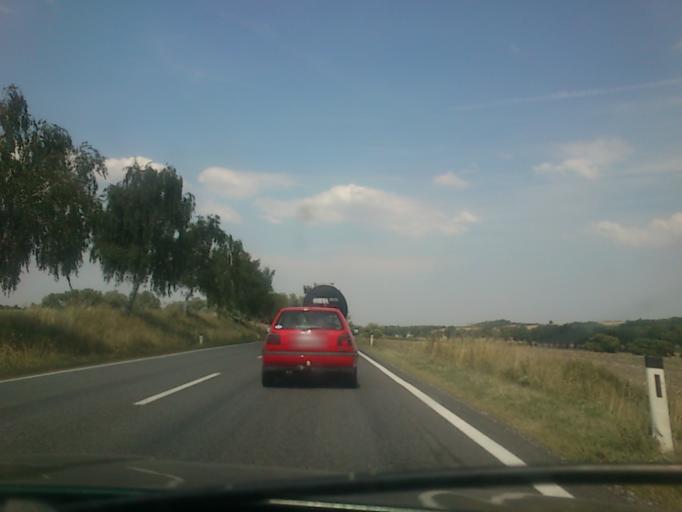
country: AT
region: Lower Austria
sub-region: Politischer Bezirk Mistelbach
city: Wilfersdorf
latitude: 48.6100
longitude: 16.6482
